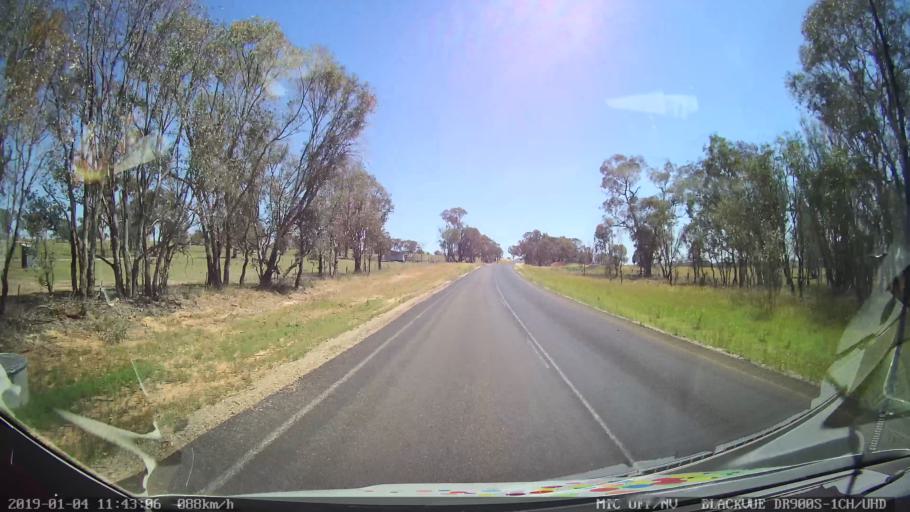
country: AU
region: New South Wales
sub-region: Cabonne
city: Molong
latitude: -32.9732
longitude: 148.7844
